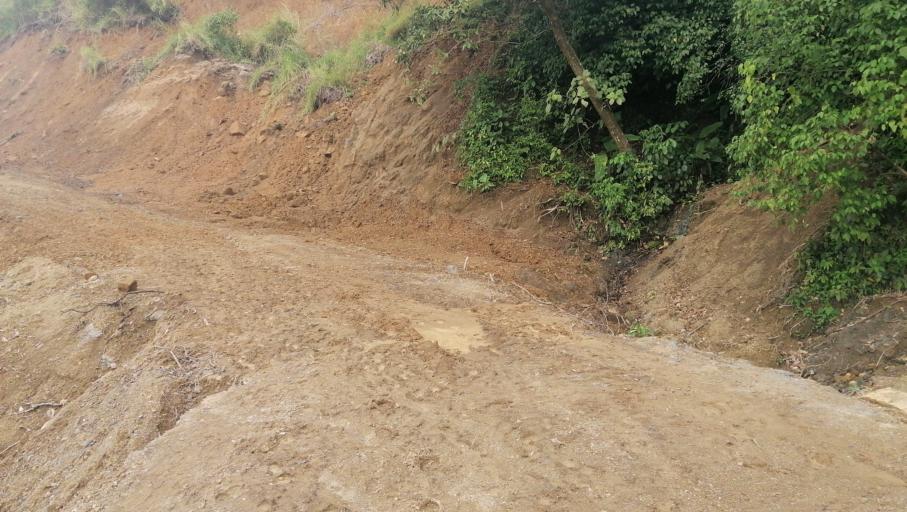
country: MX
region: Chiapas
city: Ostuacan
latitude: 17.3581
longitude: -93.3206
